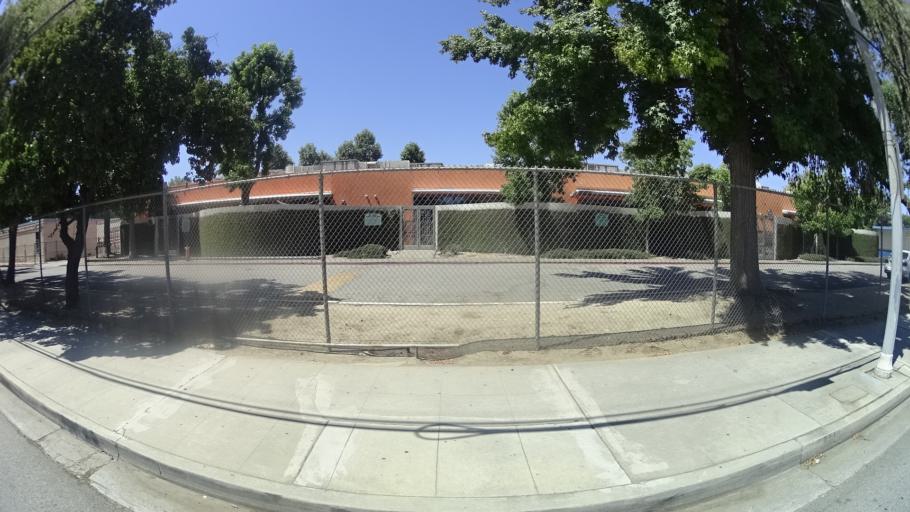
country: US
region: California
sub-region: Los Angeles County
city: Northridge
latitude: 34.1867
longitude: -118.5063
